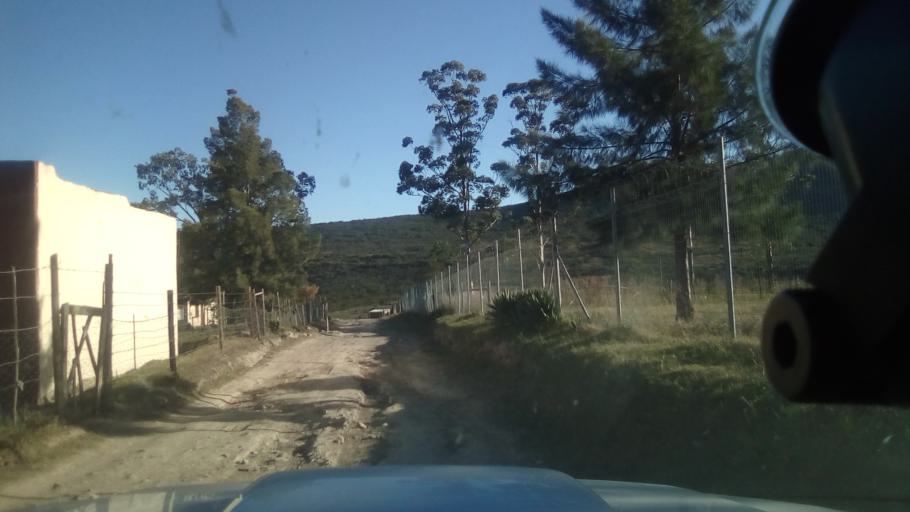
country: ZA
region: Eastern Cape
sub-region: Buffalo City Metropolitan Municipality
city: Bhisho
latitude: -32.7340
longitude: 27.3609
